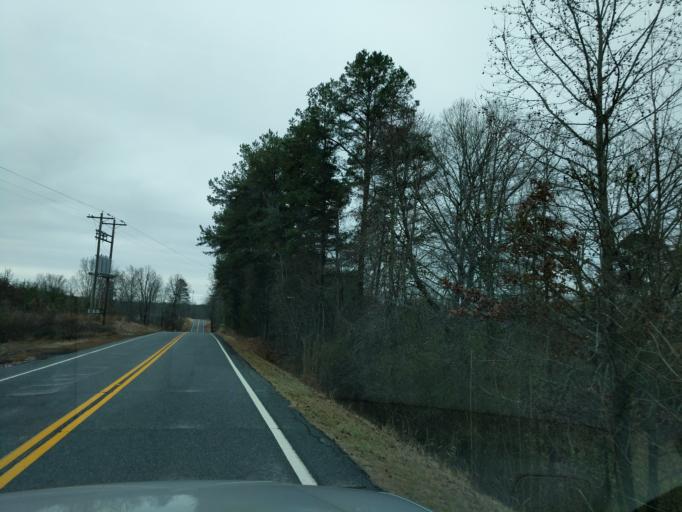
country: US
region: South Carolina
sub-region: Oconee County
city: Walhalla
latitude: 34.8212
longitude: -83.0468
